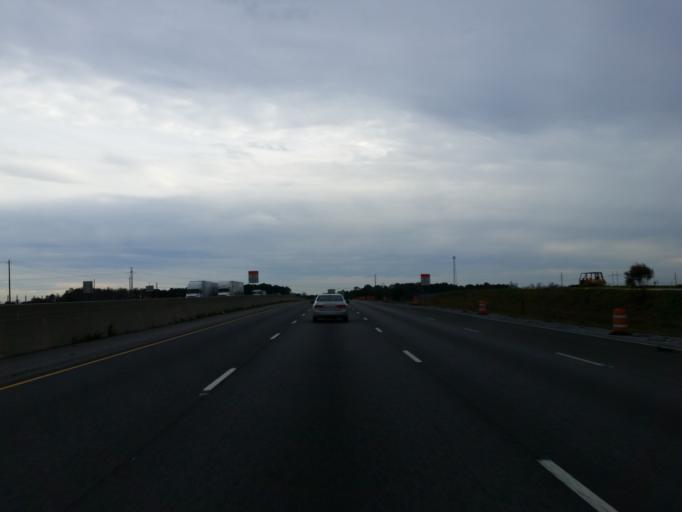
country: US
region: Georgia
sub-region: Tift County
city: Tifton
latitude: 31.5026
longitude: -83.5155
